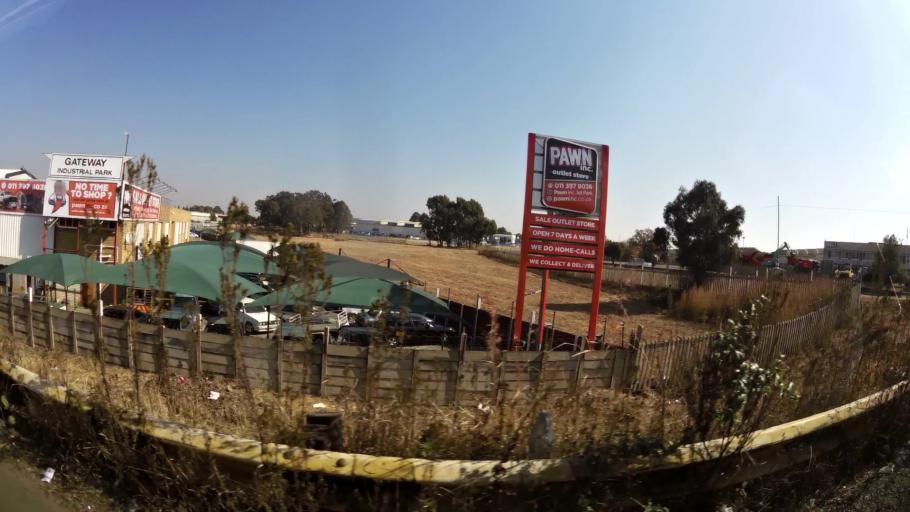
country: ZA
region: Gauteng
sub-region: Ekurhuleni Metropolitan Municipality
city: Boksburg
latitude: -26.1551
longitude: 28.2203
